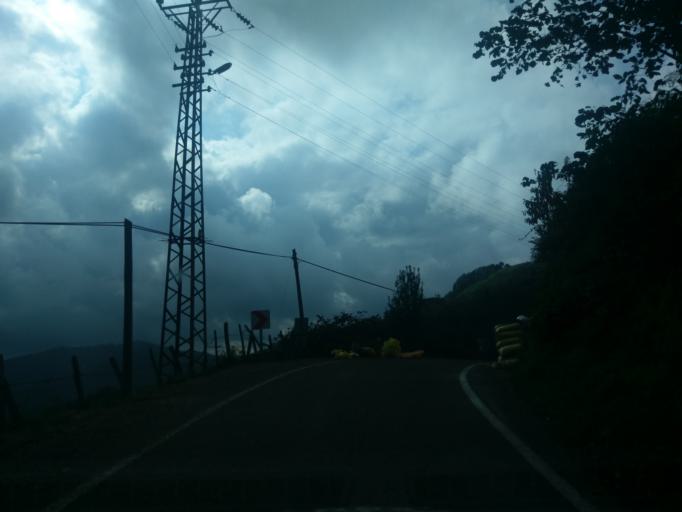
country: TR
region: Ordu
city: Camas
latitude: 40.8904
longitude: 37.6158
